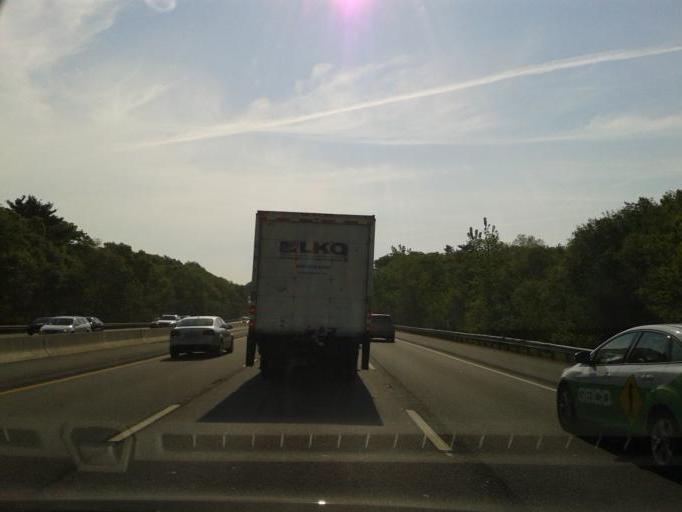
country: US
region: Massachusetts
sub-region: Middlesex County
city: Weston
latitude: 42.3352
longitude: -71.3056
